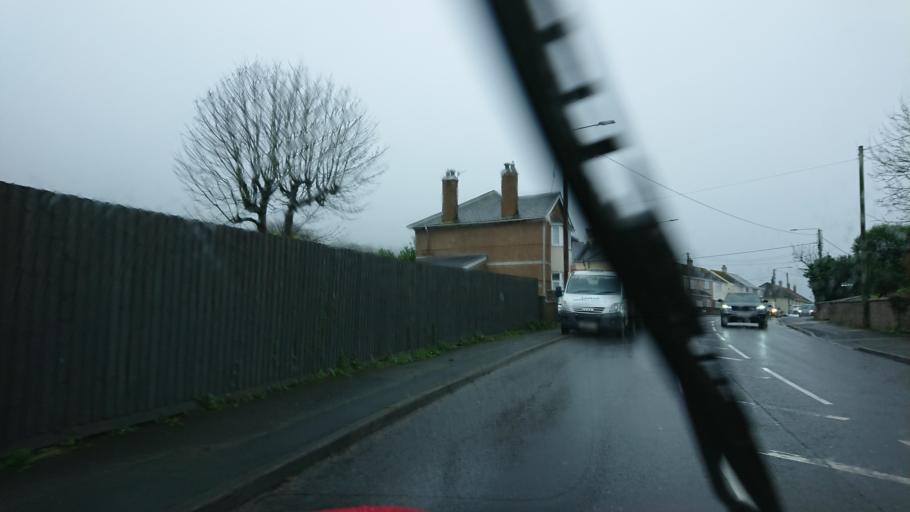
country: GB
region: England
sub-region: Plymouth
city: Plymstock
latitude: 50.3519
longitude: -4.1046
